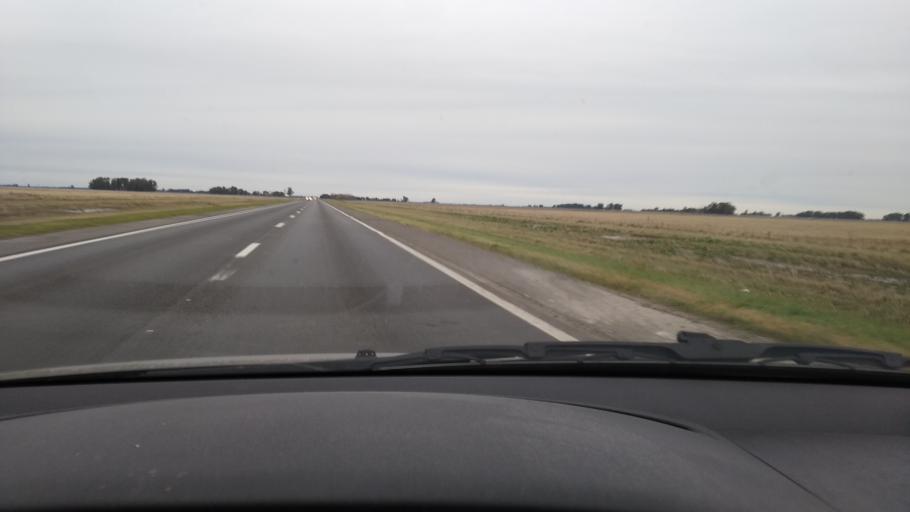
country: AR
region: Buenos Aires
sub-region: Partido de Las Flores
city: Las Flores
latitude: -36.1581
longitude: -59.2192
